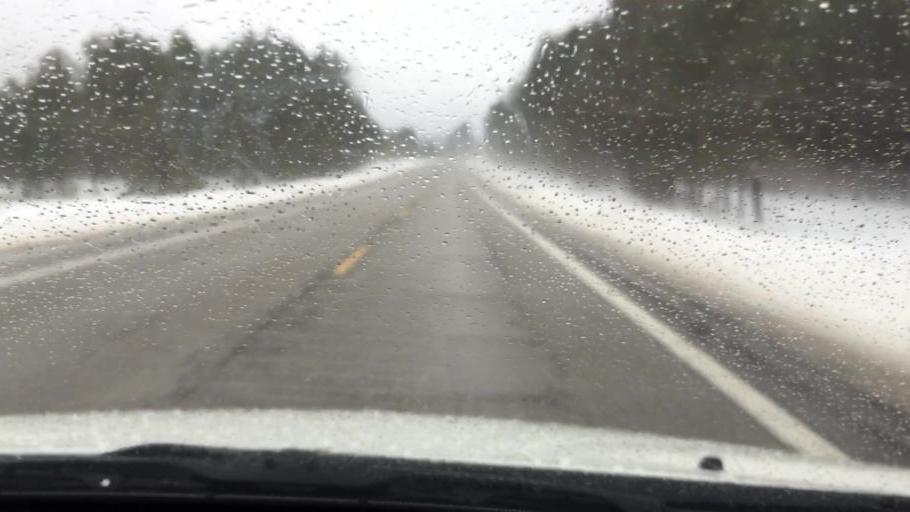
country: US
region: Michigan
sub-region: Charlevoix County
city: East Jordan
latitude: 45.0959
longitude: -85.1036
